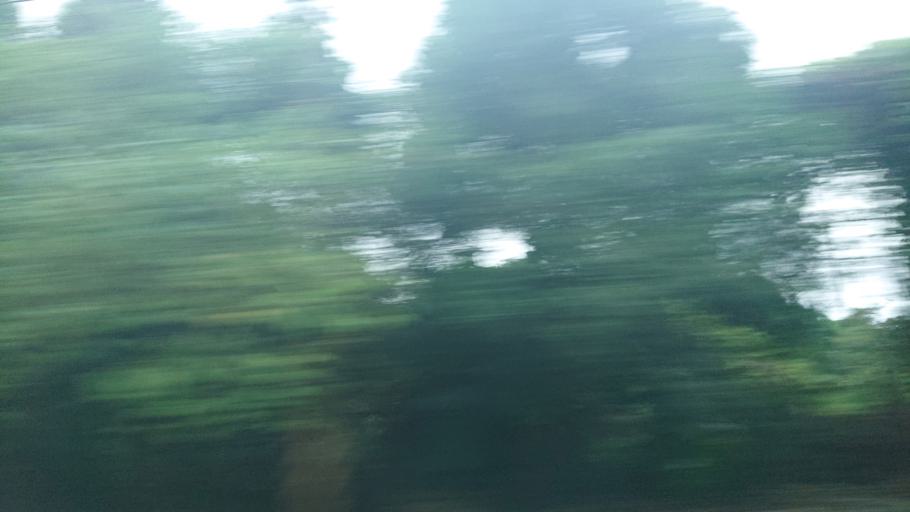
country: TW
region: Taiwan
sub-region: Chiayi
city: Jiayi Shi
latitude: 23.4779
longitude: 120.7169
